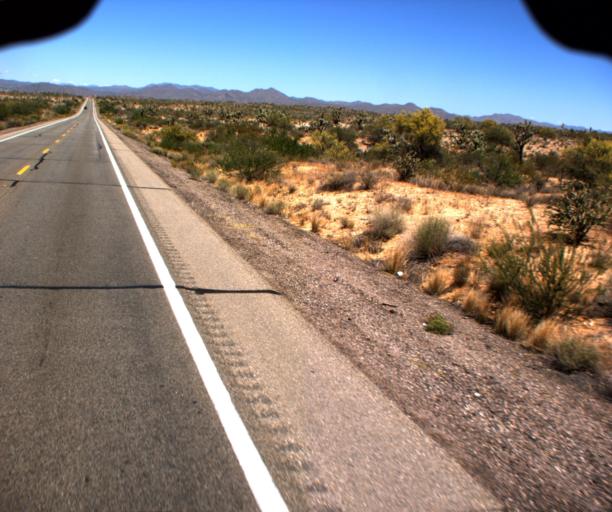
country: US
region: Arizona
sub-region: Yavapai County
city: Bagdad
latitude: 34.3255
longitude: -113.1388
